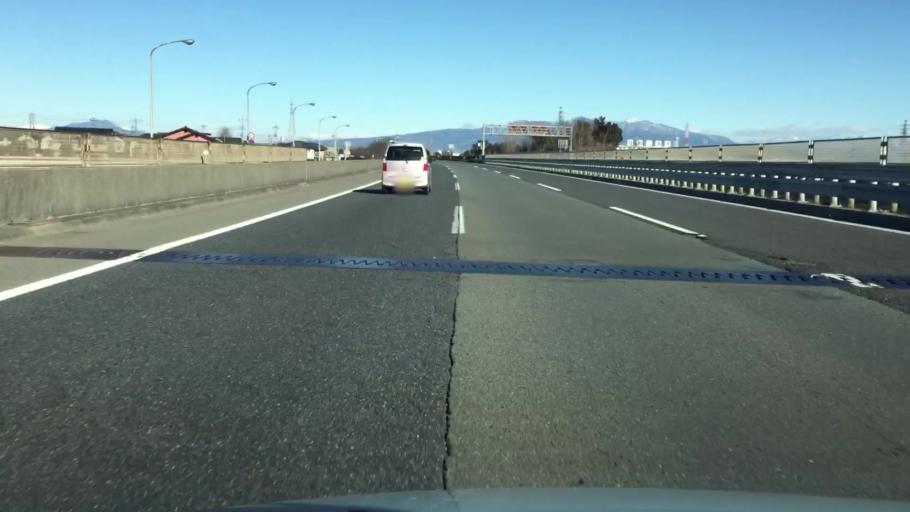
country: JP
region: Gunma
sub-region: Sawa-gun
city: Tamamura
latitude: 36.2866
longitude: 139.0980
